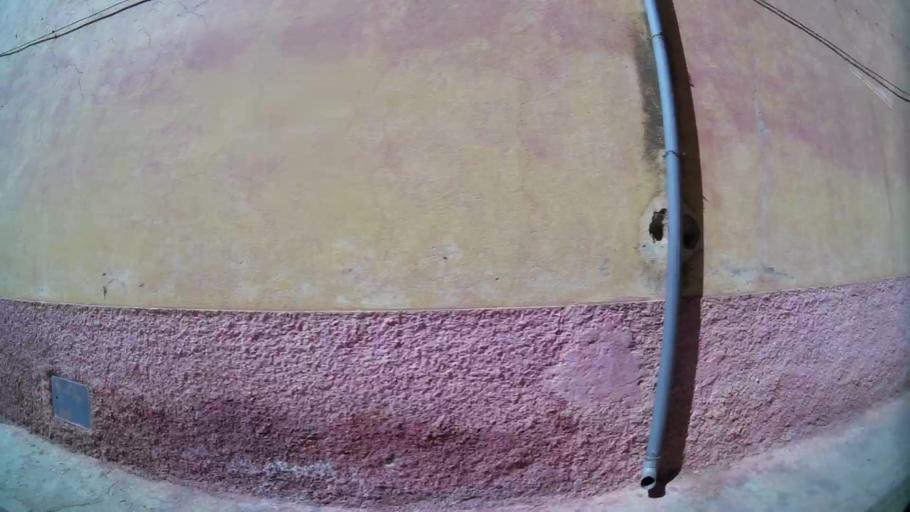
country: MA
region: Oriental
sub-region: Oujda-Angad
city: Oujda
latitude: 34.6808
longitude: -1.9270
